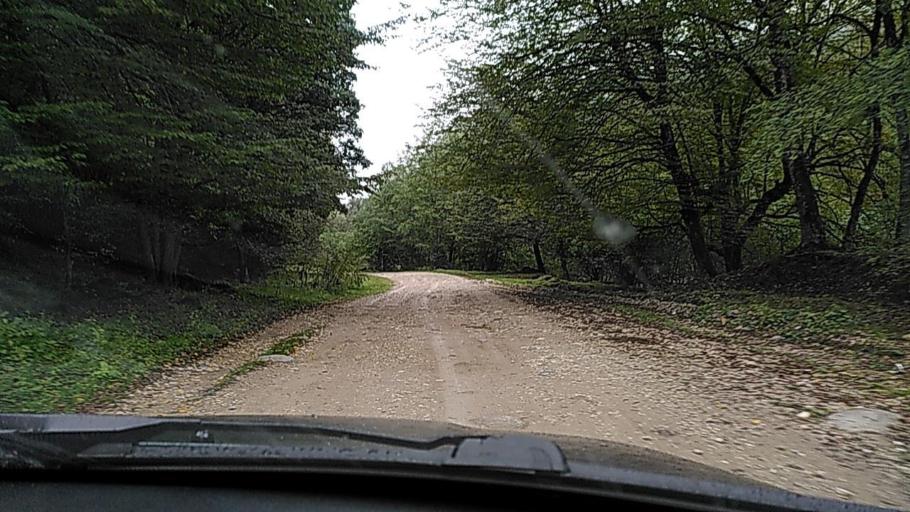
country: RU
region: Kabardino-Balkariya
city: Belaya Rechka
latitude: 43.4135
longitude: 43.4736
